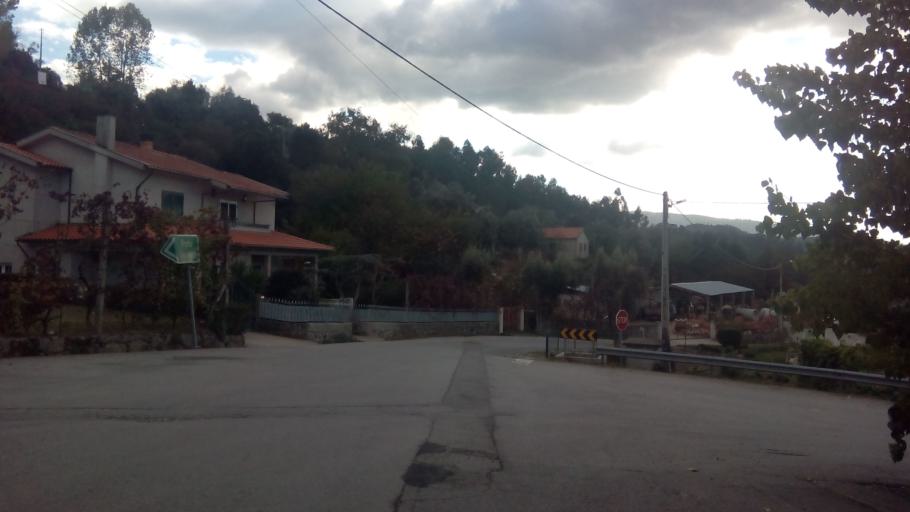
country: PT
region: Porto
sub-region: Amarante
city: Amarante
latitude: 41.2783
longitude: -7.9927
